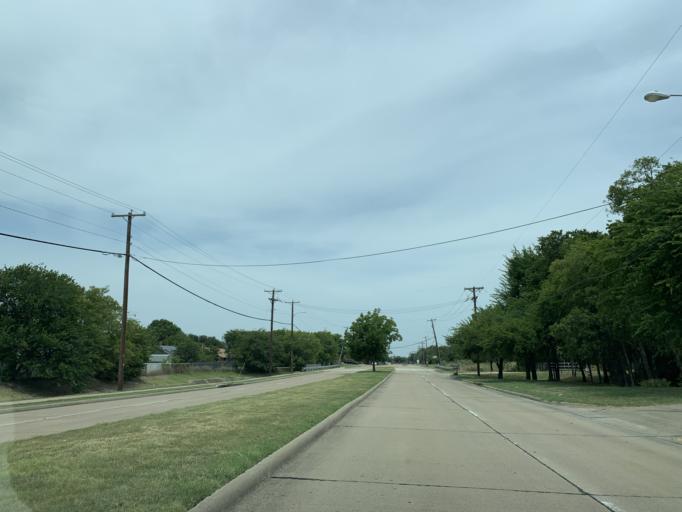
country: US
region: Texas
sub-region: Dallas County
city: Cedar Hill
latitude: 32.6540
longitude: -97.0148
